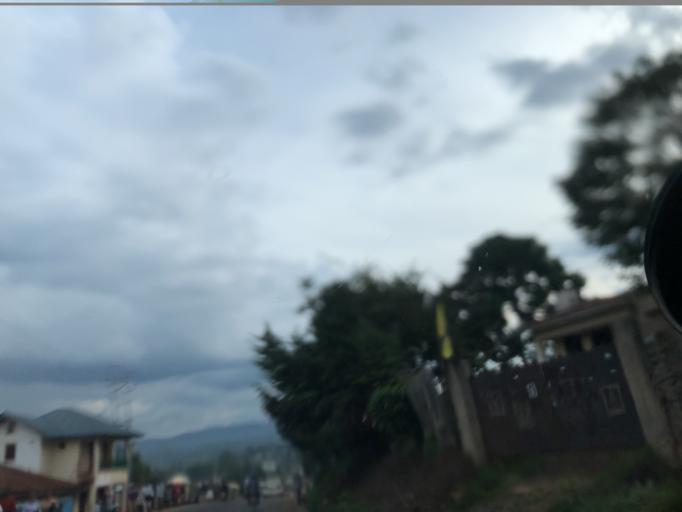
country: CD
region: South Kivu
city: Bukavu
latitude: -2.3001
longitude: 28.7975
